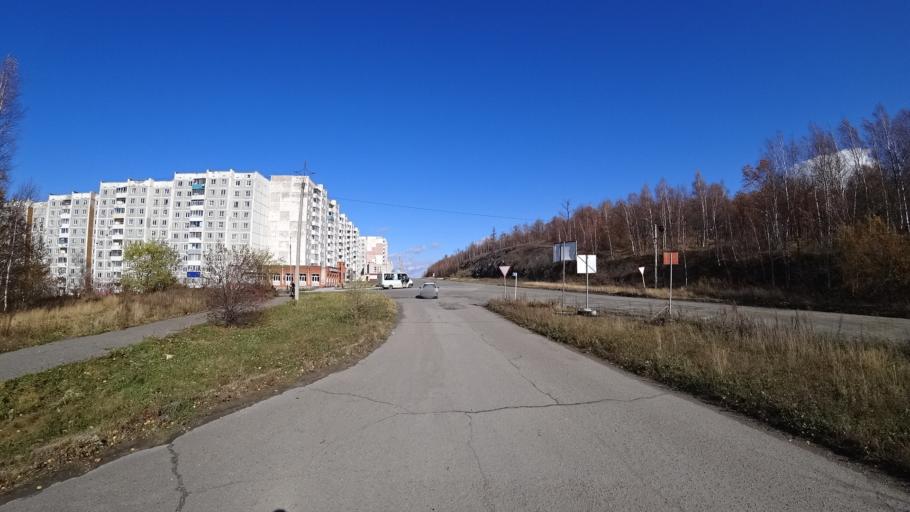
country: RU
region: Khabarovsk Krai
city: Amursk
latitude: 50.2421
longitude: 136.9199
